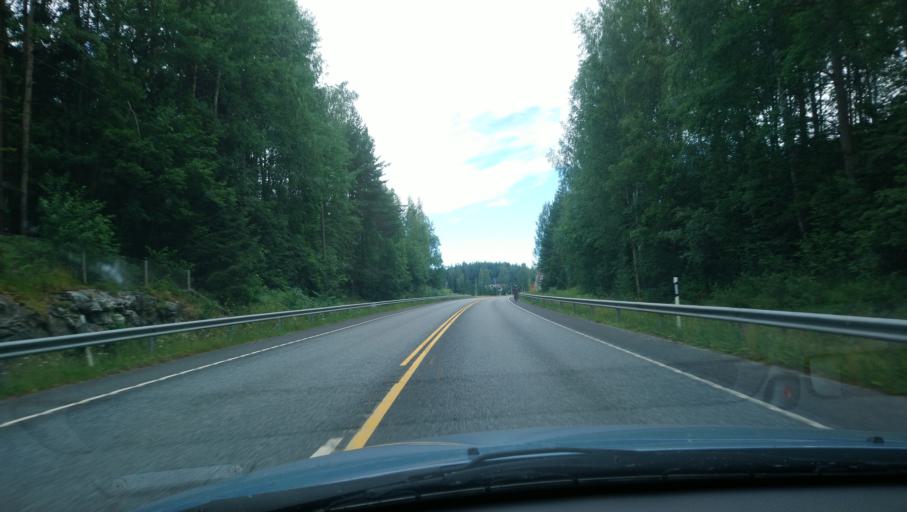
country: FI
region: Uusimaa
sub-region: Porvoo
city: Porvoo
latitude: 60.4193
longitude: 25.5790
